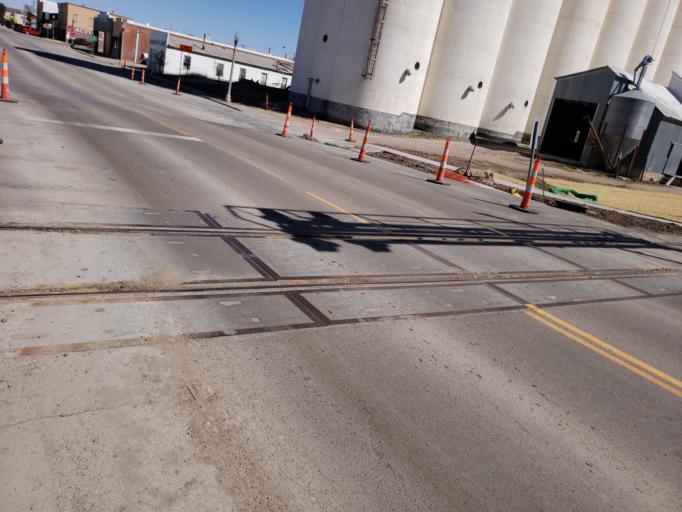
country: US
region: Kansas
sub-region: Ness County
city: Ness City
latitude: 38.4516
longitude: -99.9051
